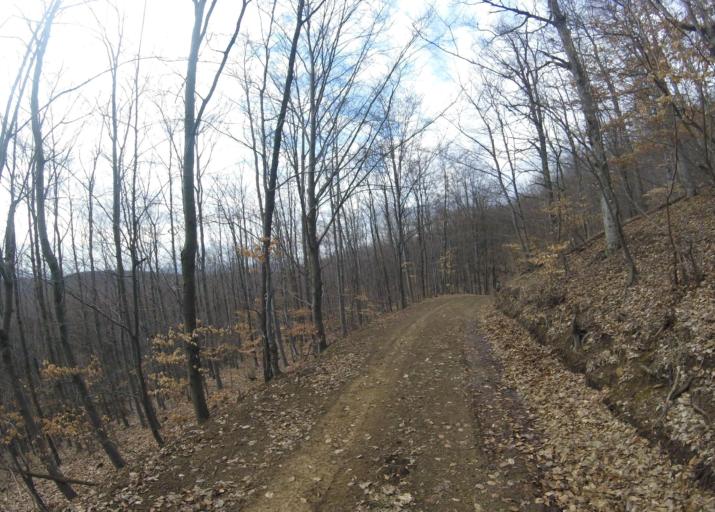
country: HU
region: Heves
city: Belapatfalva
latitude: 48.0268
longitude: 20.3711
